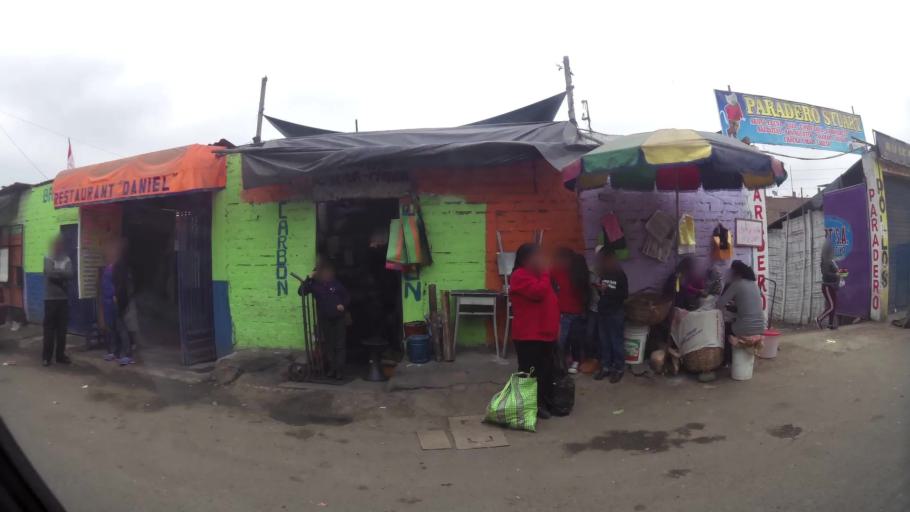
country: PE
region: Lima
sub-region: Provincia de Huaral
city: Huaral
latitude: -11.5022
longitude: -77.2059
